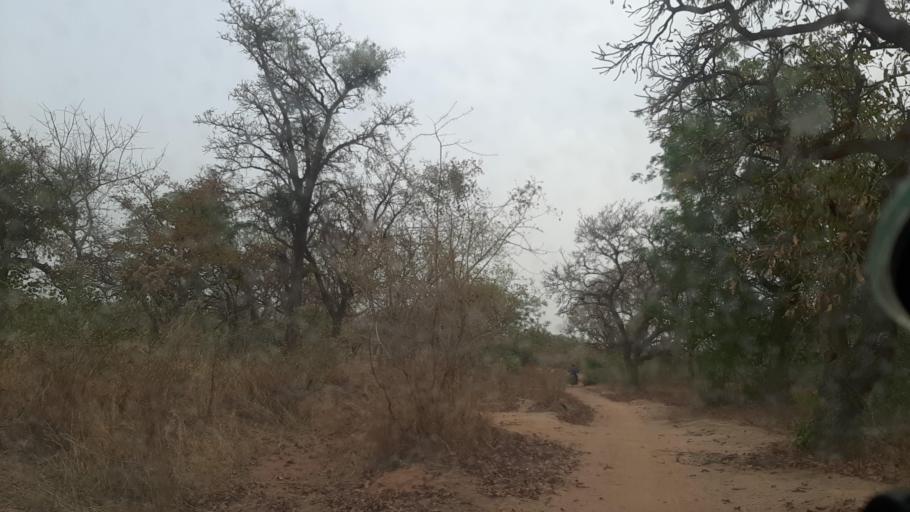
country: BF
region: Boucle du Mouhoun
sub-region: Province des Banwa
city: Salanso
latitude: 11.8580
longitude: -4.4324
